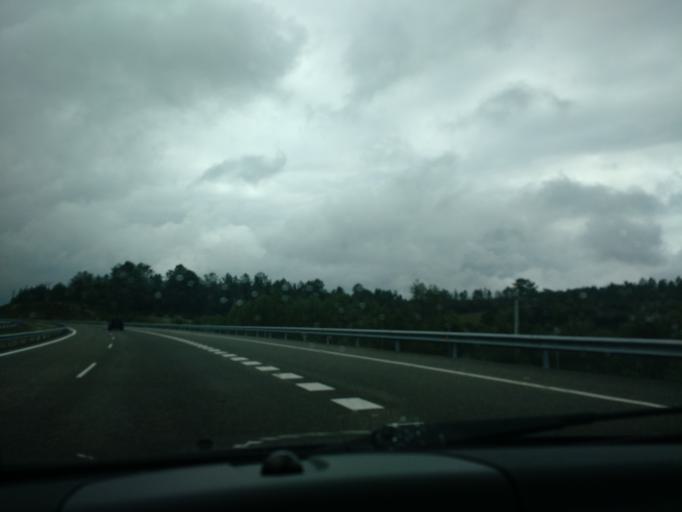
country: ES
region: Galicia
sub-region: Provincia da Coruna
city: Oroso
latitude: 42.9411
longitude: -8.4615
